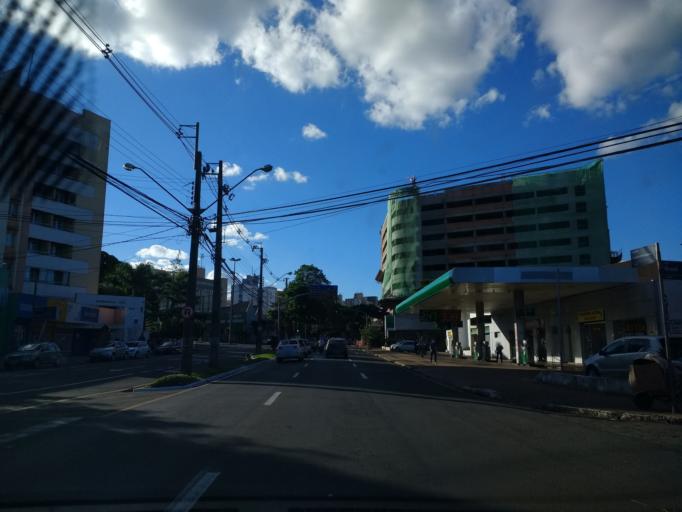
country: BR
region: Parana
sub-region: Londrina
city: Londrina
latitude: -23.3277
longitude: -51.1539
